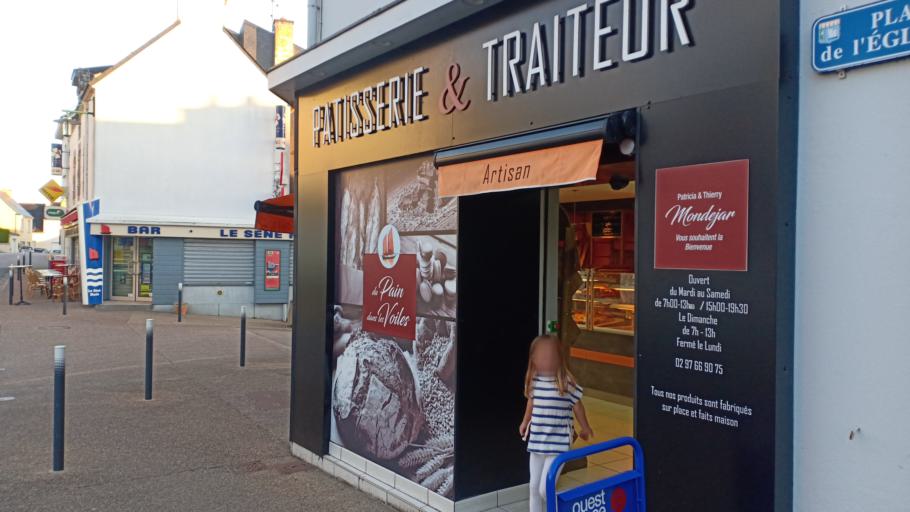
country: FR
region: Brittany
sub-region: Departement du Morbihan
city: Sene
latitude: 47.6195
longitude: -2.7366
